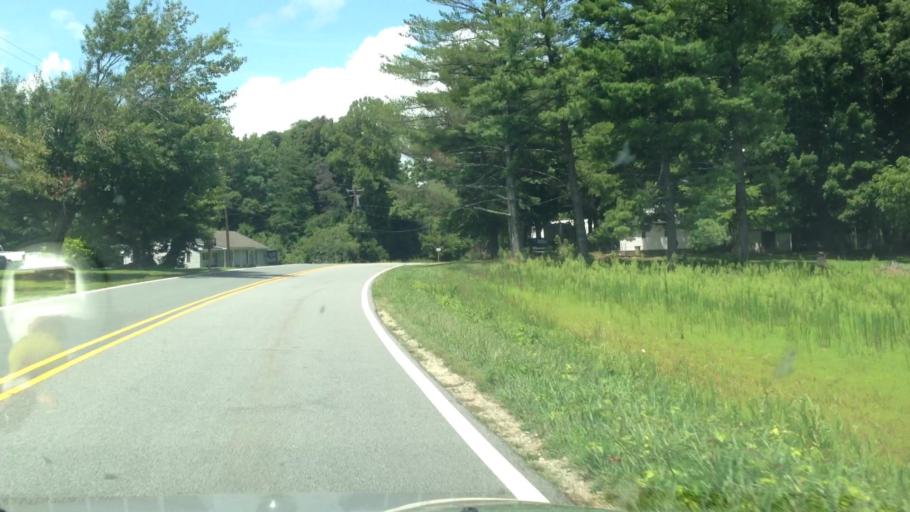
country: US
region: North Carolina
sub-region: Forsyth County
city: Kernersville
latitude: 36.1472
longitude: -80.0876
